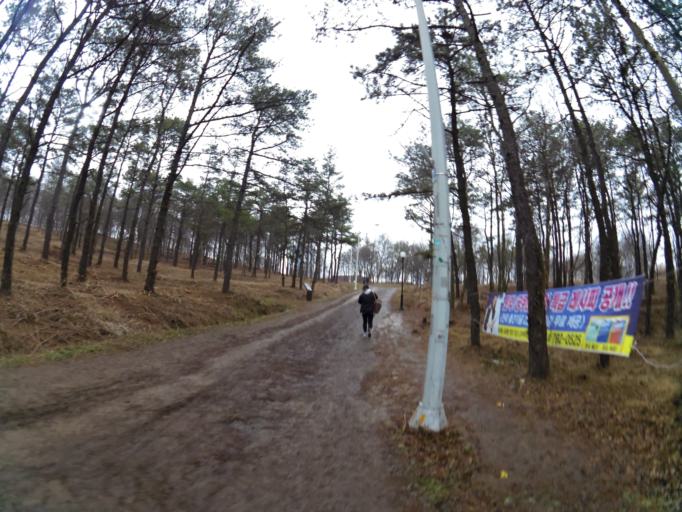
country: KR
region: Gyeongsangbuk-do
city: Gyeongsan-si
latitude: 35.8366
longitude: 128.7575
